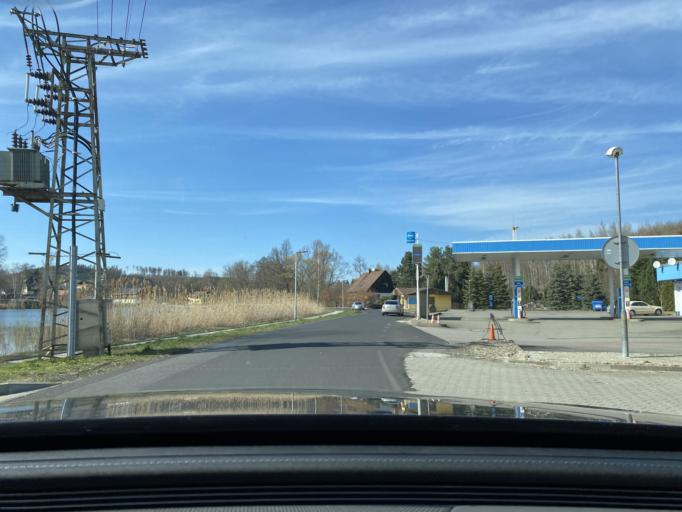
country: CZ
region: Ustecky
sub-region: Okres Decin
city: Sluknov
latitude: 51.0314
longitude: 14.4512
